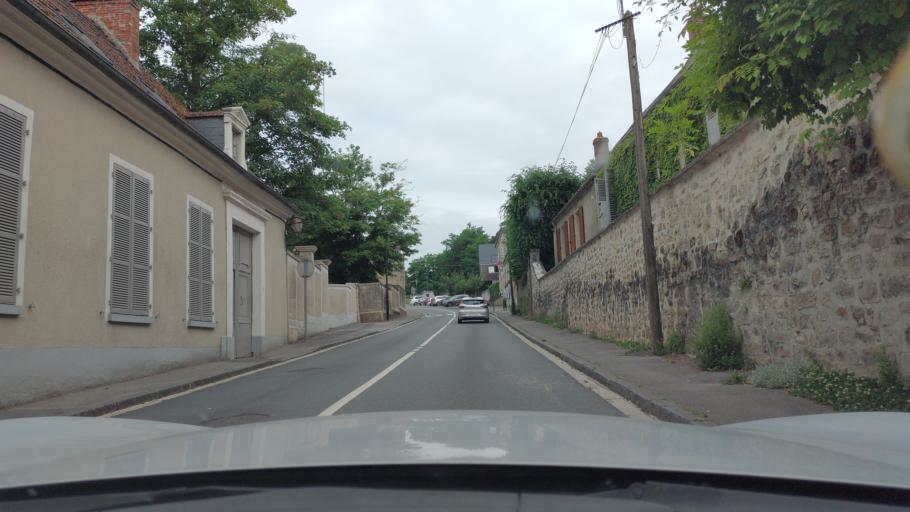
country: FR
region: Picardie
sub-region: Departement de l'Oise
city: Betz
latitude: 49.1568
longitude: 2.9541
